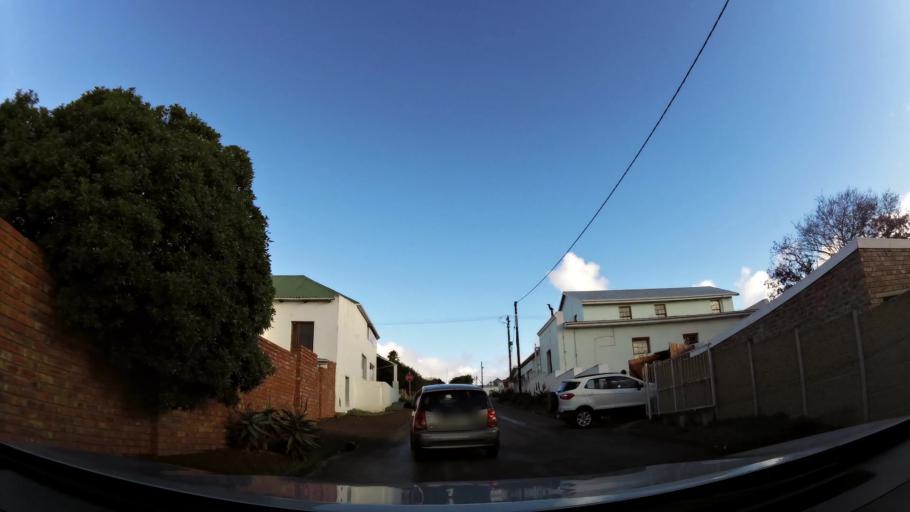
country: ZA
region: Western Cape
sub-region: Eden District Municipality
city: Riversdale
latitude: -34.2030
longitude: 21.5866
